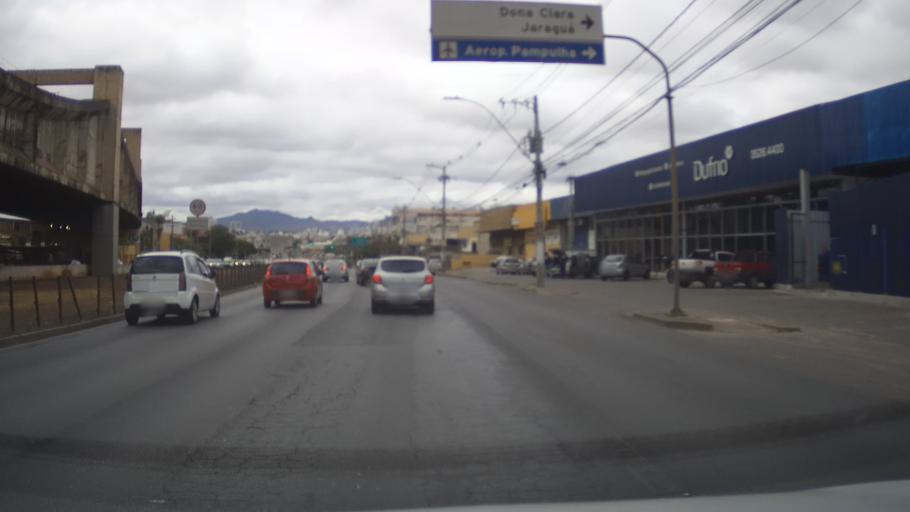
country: BR
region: Minas Gerais
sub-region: Belo Horizonte
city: Belo Horizonte
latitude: -19.8562
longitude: -43.9352
